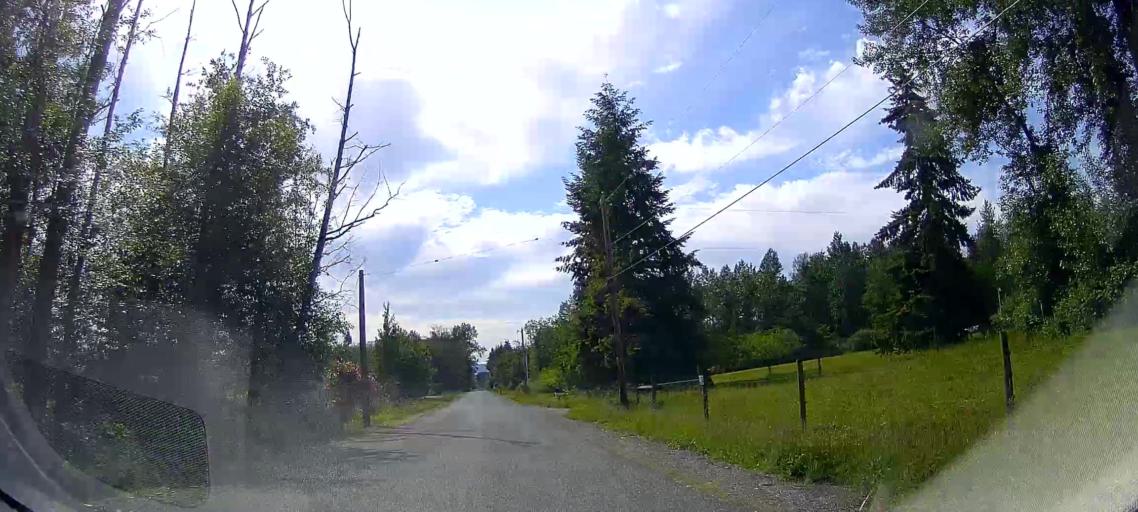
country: US
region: Washington
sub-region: Skagit County
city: Burlington
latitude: 48.5448
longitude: -122.3675
